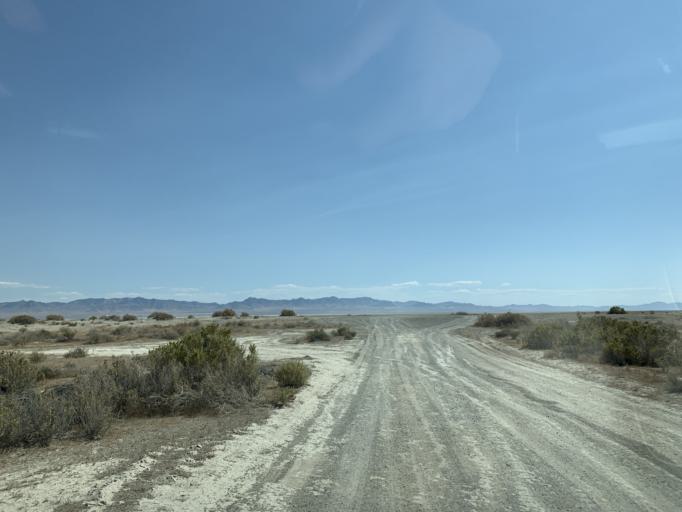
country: US
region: Utah
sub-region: Millard County
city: Delta
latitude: 39.0816
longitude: -113.1865
